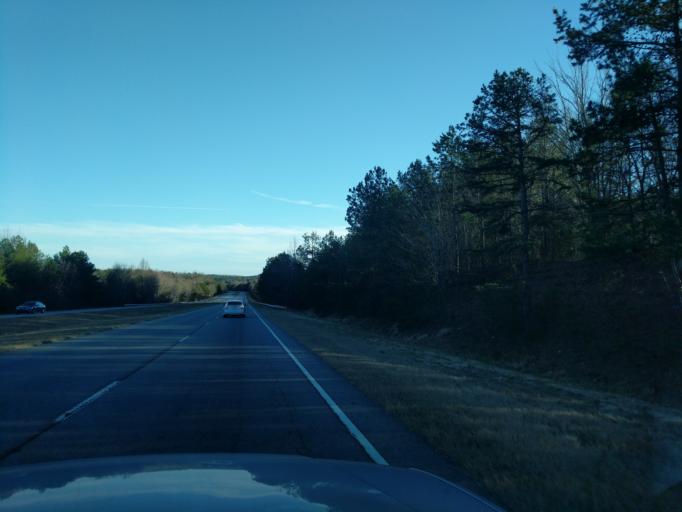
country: US
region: Georgia
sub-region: Stephens County
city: Toccoa
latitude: 34.5752
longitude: -83.4049
